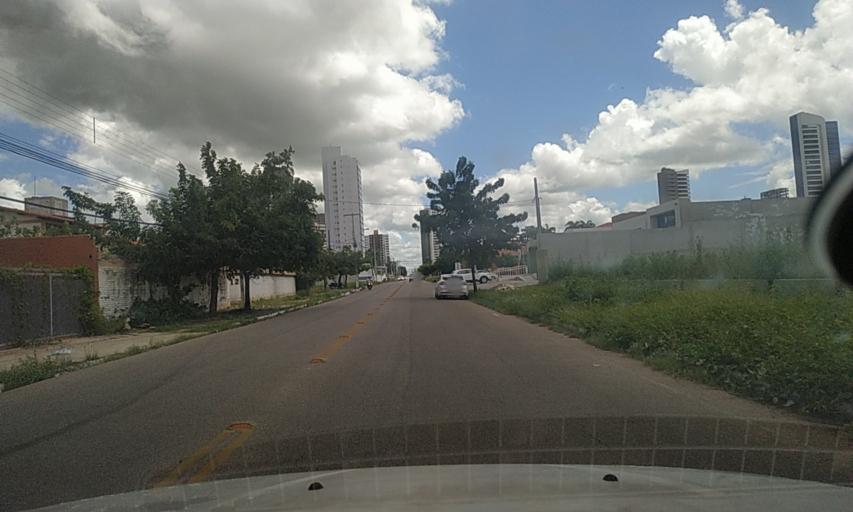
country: BR
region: Rio Grande do Norte
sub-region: Mossoro
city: Mossoro
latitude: -5.1821
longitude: -37.3568
